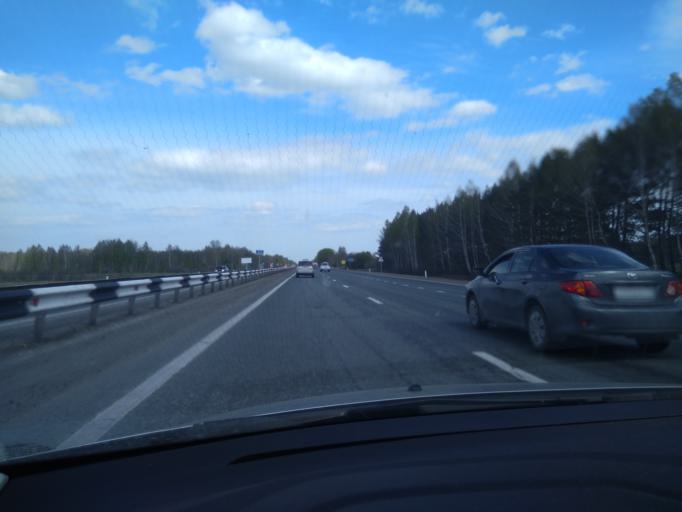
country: RU
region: Tjumen
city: Moskovskiy
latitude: 57.1048
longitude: 65.3416
